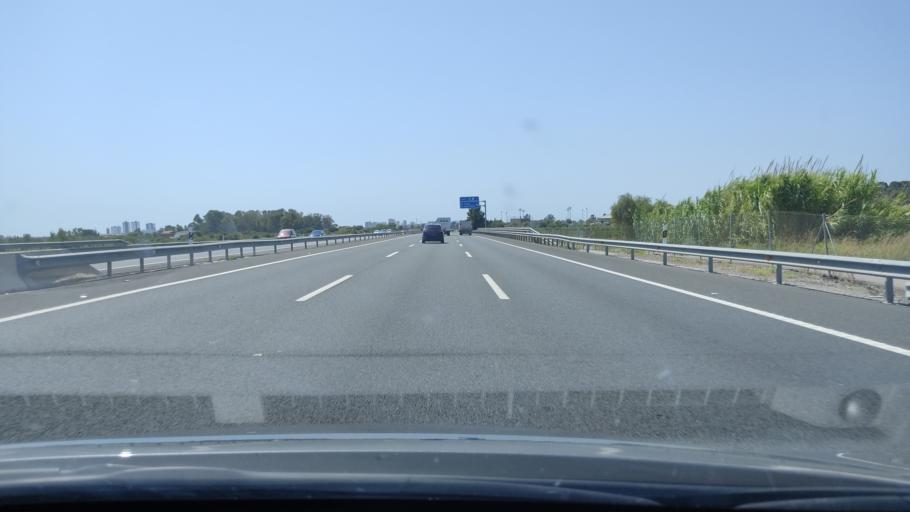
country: ES
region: Valencia
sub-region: Provincia de Valencia
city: Puig
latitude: 39.6007
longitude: -0.2934
